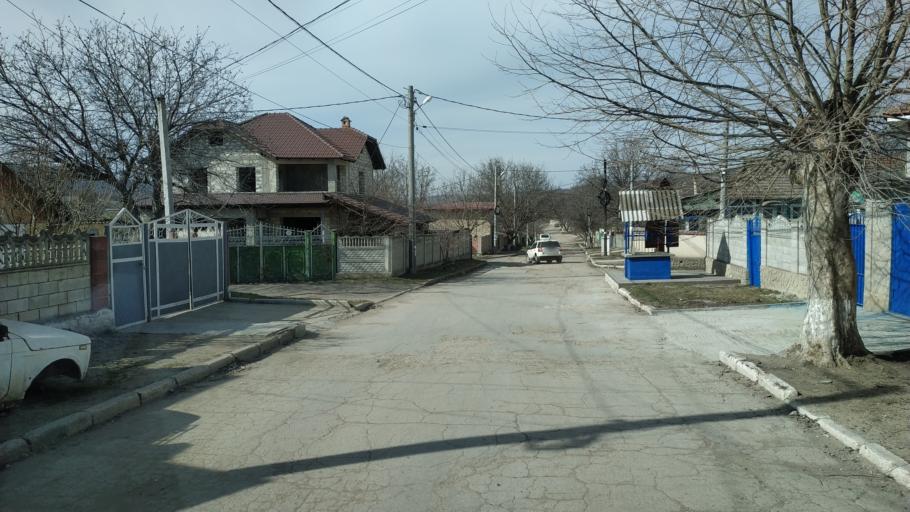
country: MD
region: Straseni
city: Straseni
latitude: 47.0971
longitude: 28.6558
